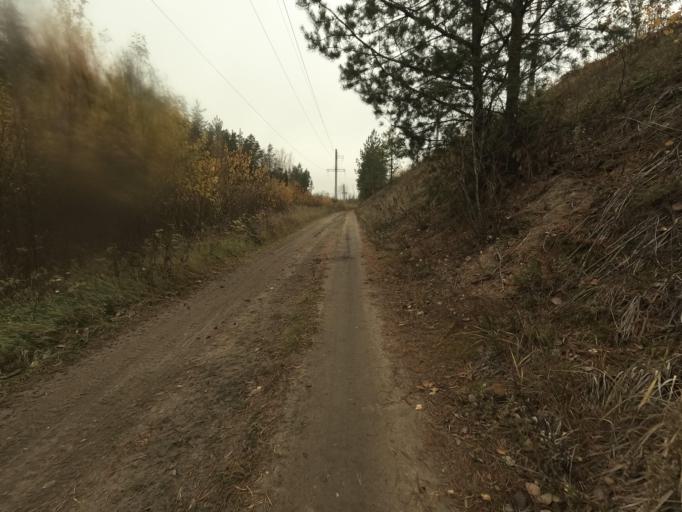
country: RU
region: Leningrad
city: Pavlovo
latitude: 59.7697
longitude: 30.9098
